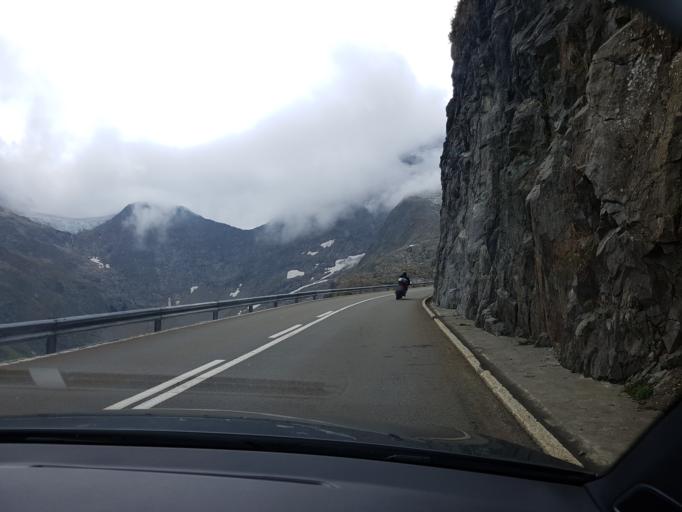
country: CH
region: Obwalden
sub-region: Obwalden
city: Engelberg
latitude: 46.7368
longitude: 8.4515
